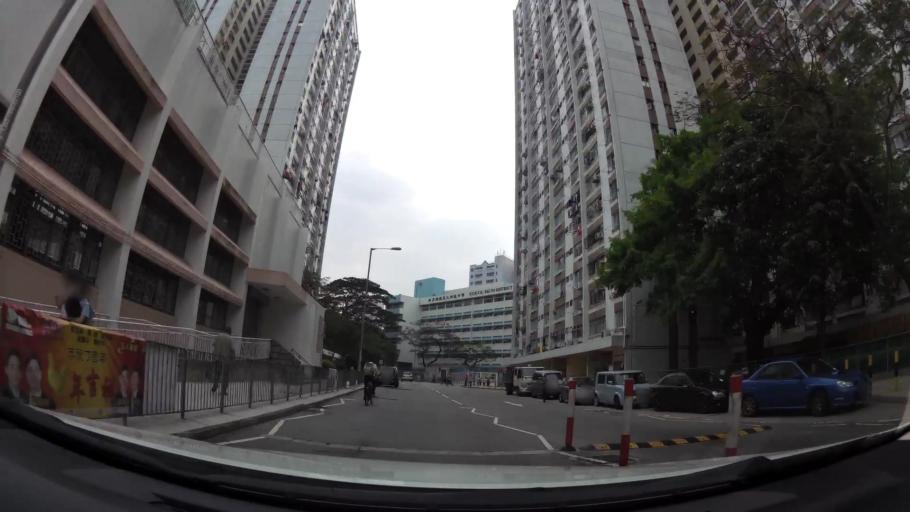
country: HK
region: Tai Po
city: Tai Po
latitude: 22.4557
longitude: 114.1688
